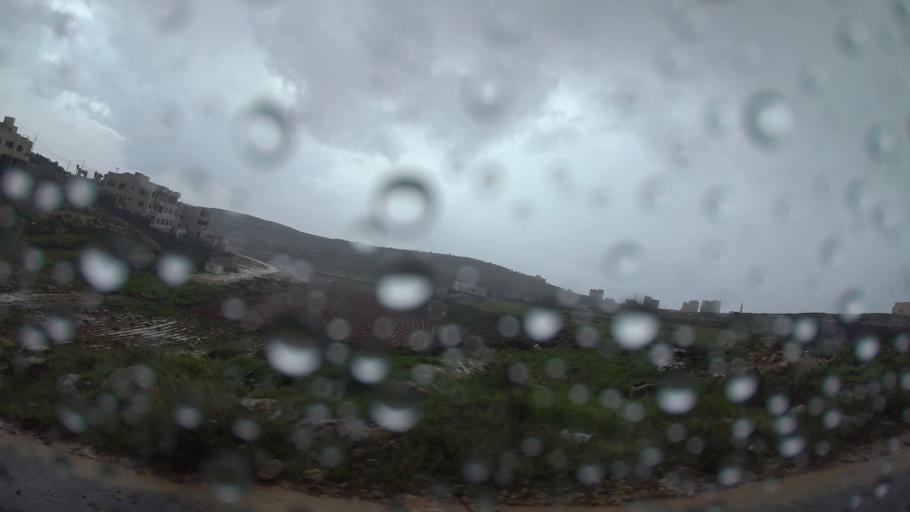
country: JO
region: Amman
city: Umm as Summaq
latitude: 31.8748
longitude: 35.8583
